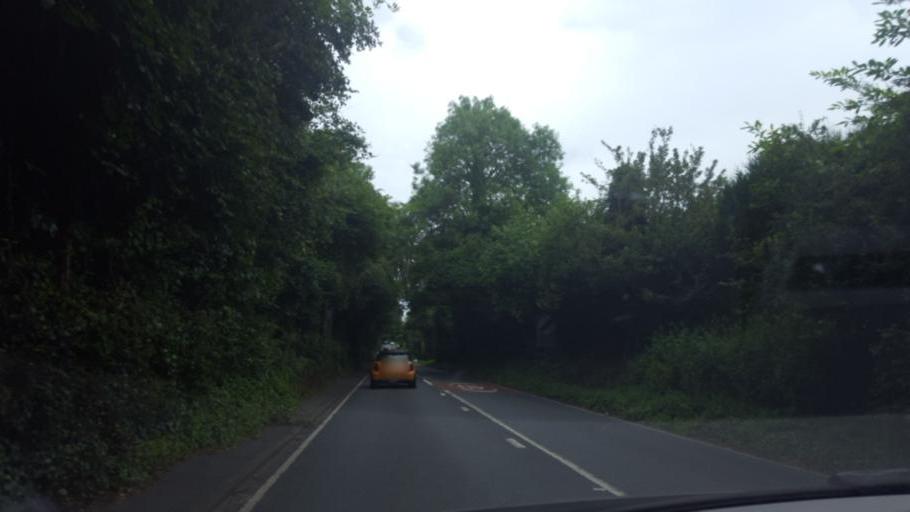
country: GB
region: England
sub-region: Royal Borough of Windsor and Maidenhead
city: Hurley
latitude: 51.5377
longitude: -0.7933
